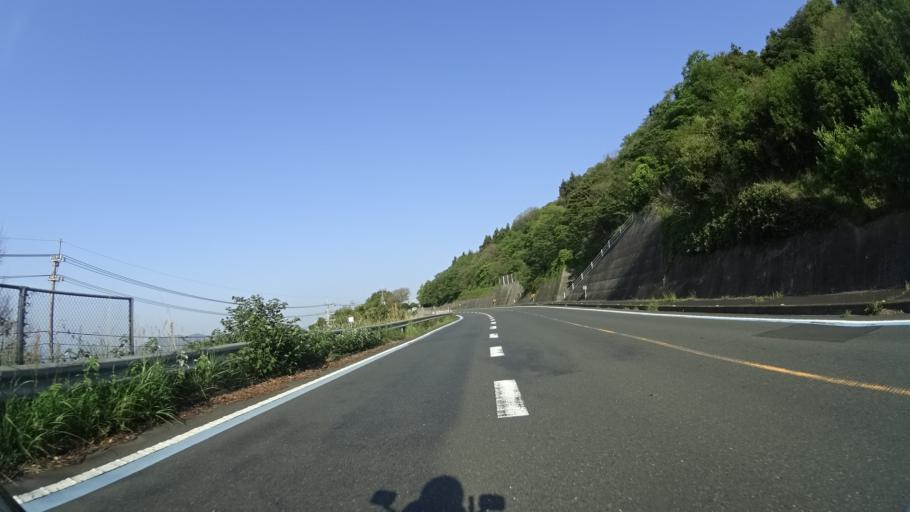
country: JP
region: Ehime
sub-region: Nishiuwa-gun
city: Ikata-cho
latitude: 33.4817
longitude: 132.3144
